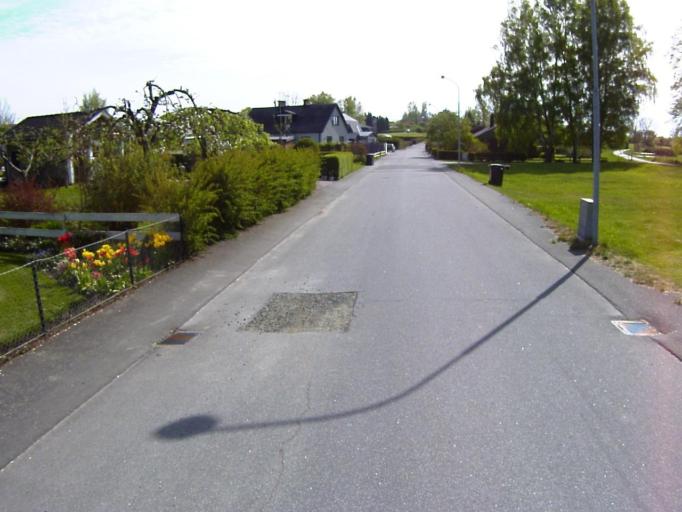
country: SE
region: Skane
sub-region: Kristianstads Kommun
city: Fjalkinge
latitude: 56.0964
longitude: 14.2456
